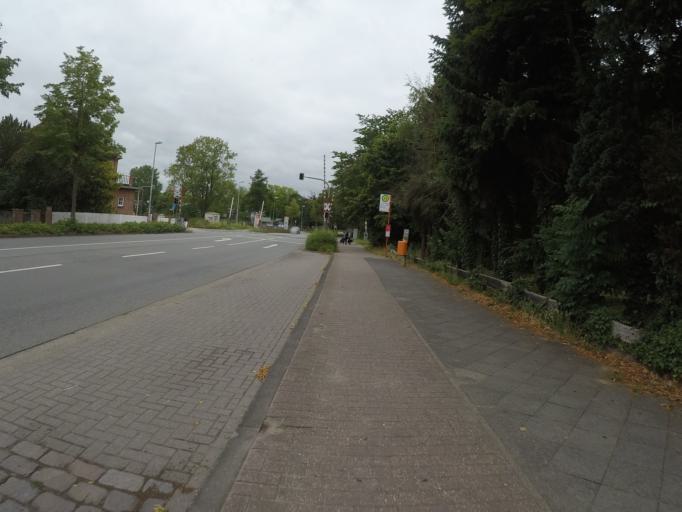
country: DE
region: Lower Saxony
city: Stade
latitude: 53.6018
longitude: 9.4842
